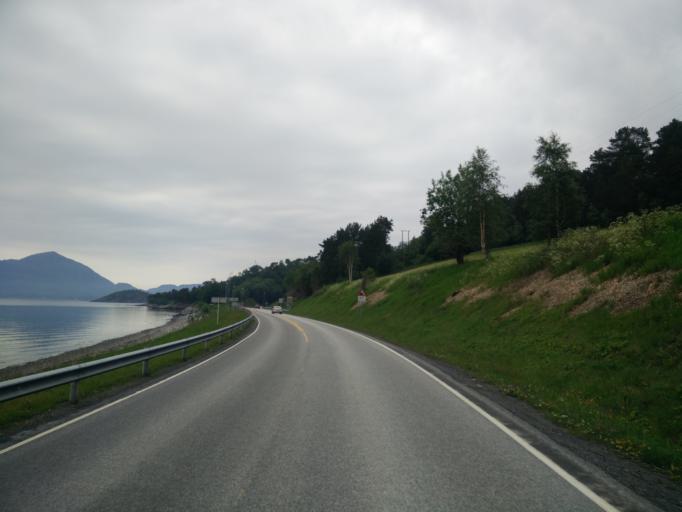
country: NO
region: More og Romsdal
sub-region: Kristiansund
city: Rensvik
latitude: 62.9786
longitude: 7.7941
